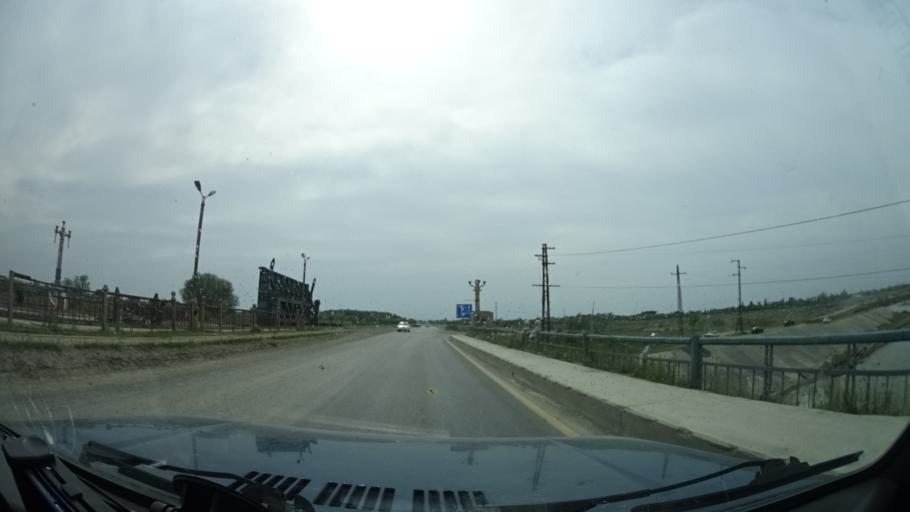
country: IR
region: Ardabil
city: Parsabad
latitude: 39.7390
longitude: 47.9726
